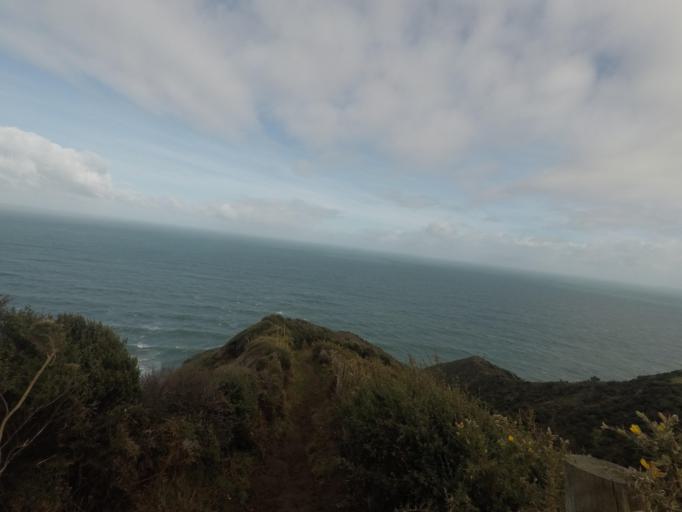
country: NZ
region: Auckland
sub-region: Auckland
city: Muriwai Beach
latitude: -36.8781
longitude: 174.4339
